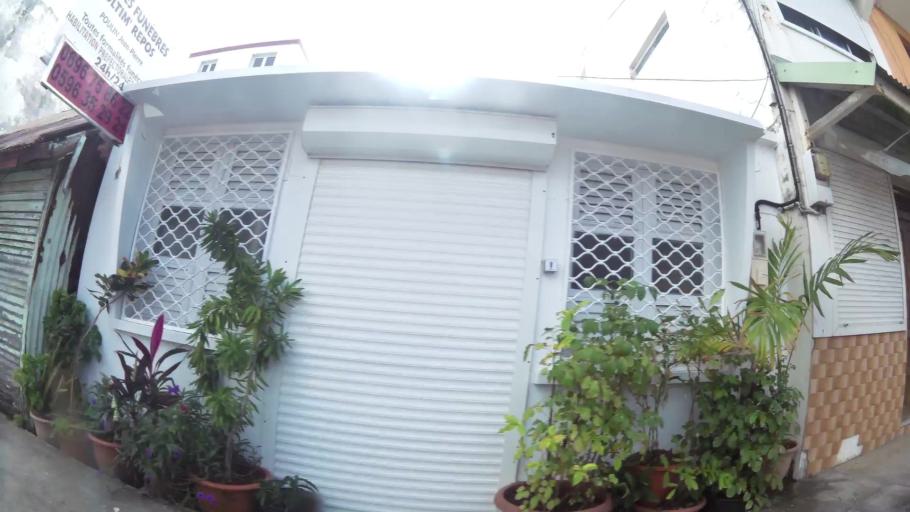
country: MQ
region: Martinique
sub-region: Martinique
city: Le Vauclin
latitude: 14.5469
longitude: -60.8377
